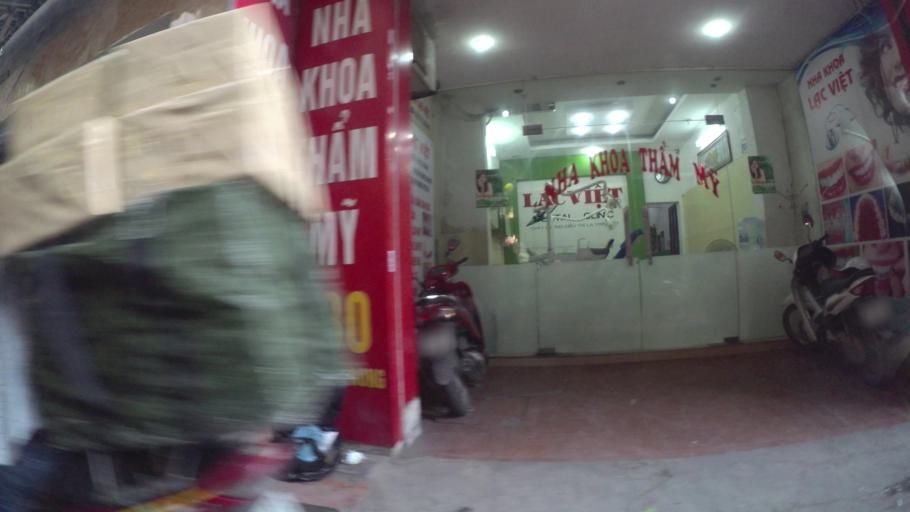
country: VN
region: Ha Noi
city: Thanh Xuan
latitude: 20.9921
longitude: 105.8173
